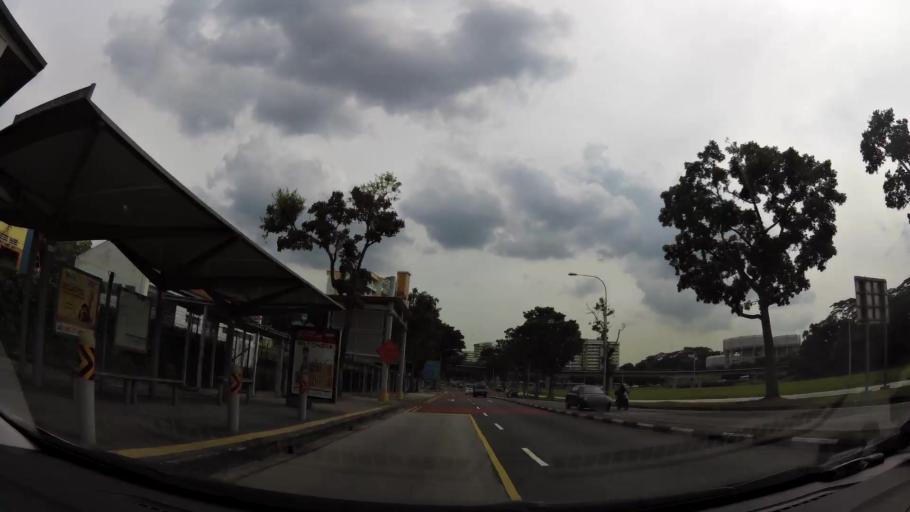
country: MY
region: Johor
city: Johor Bahru
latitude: 1.4345
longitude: 103.7726
